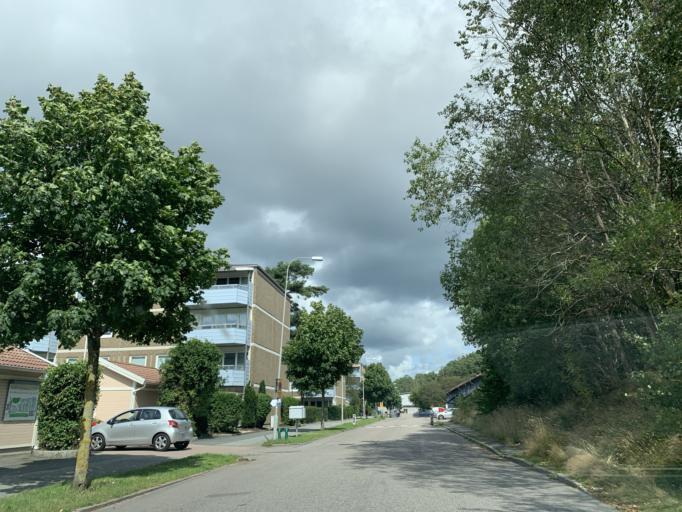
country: SE
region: Vaestra Goetaland
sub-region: Goteborg
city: Eriksbo
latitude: 57.7562
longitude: 12.0590
